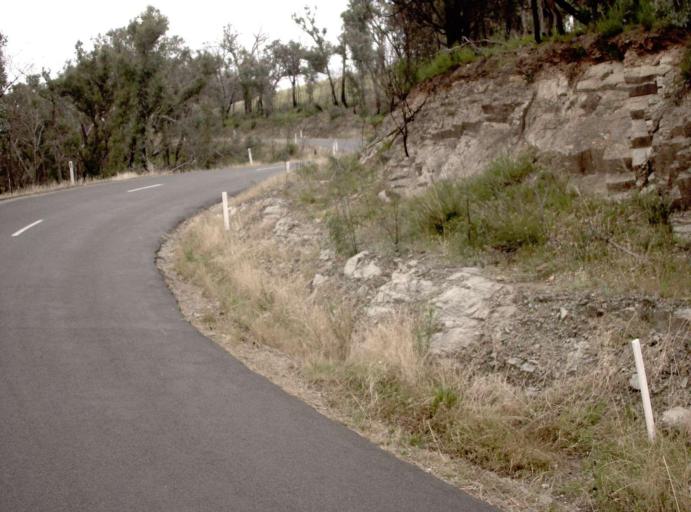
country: AU
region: Victoria
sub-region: Wellington
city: Heyfield
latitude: -37.8480
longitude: 146.7075
